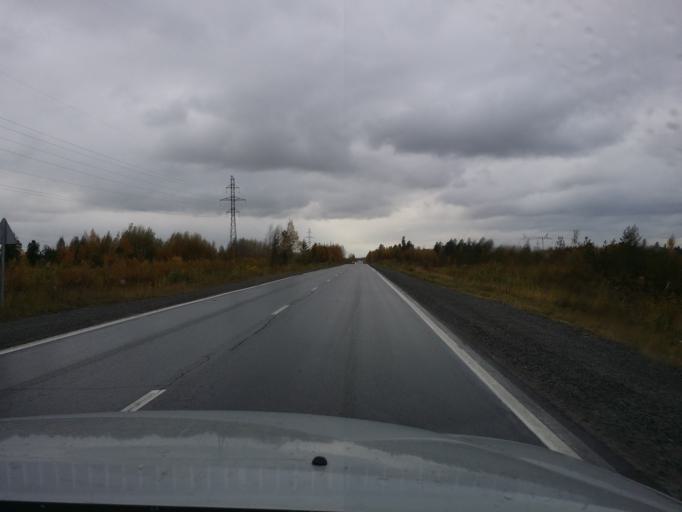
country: RU
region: Khanty-Mansiyskiy Avtonomnyy Okrug
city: Megion
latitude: 61.1042
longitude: 75.9385
